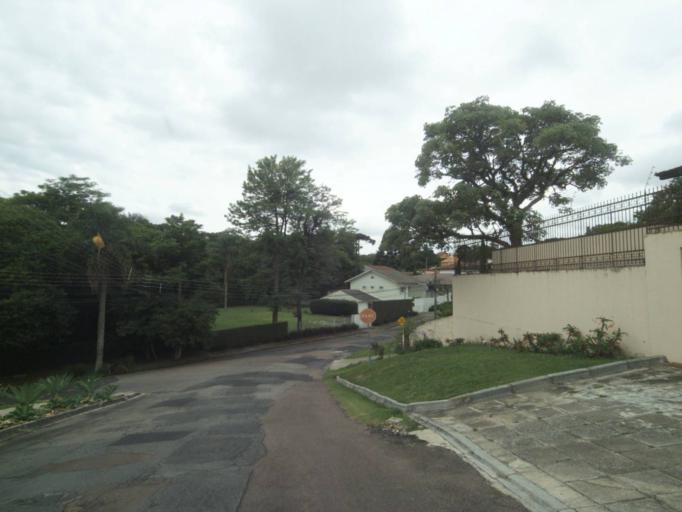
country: BR
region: Parana
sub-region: Curitiba
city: Curitiba
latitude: -25.4020
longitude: -49.2915
